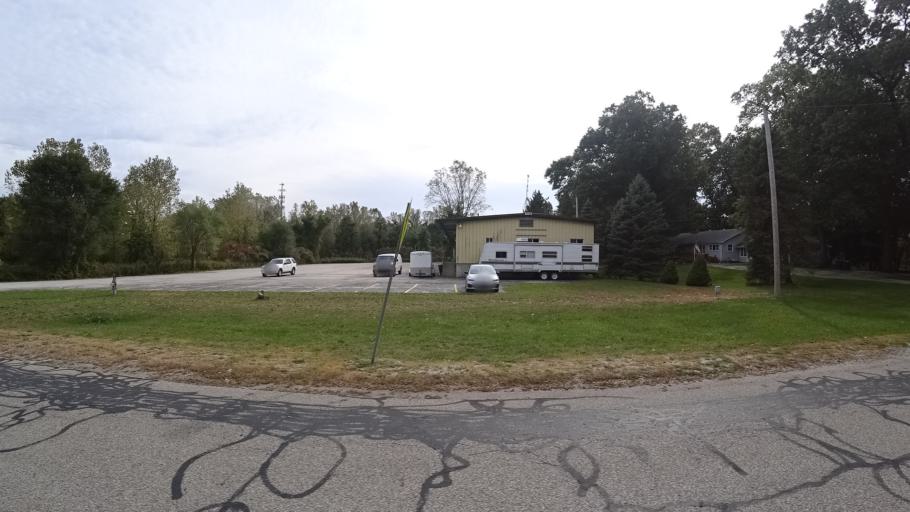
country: US
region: Indiana
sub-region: LaPorte County
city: Long Beach
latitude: 41.7383
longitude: -86.8282
